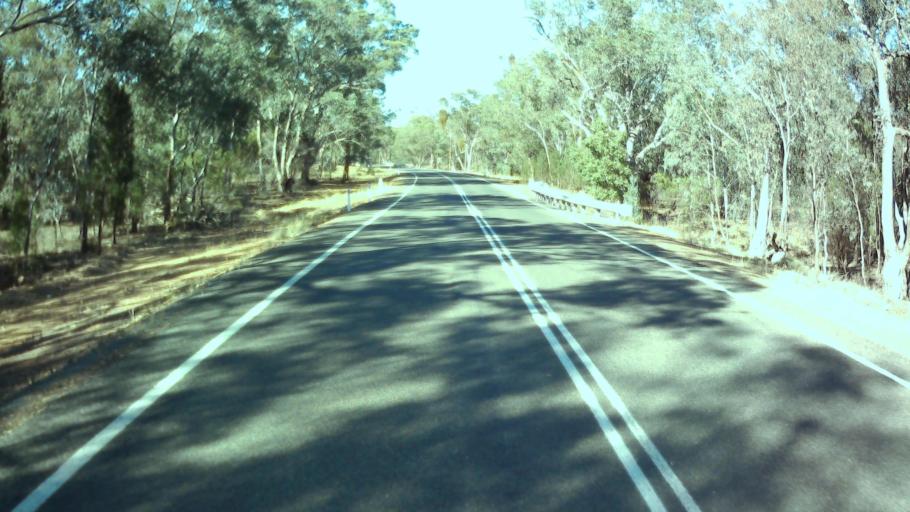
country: AU
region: New South Wales
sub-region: Weddin
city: Grenfell
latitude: -34.0019
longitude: 148.1278
